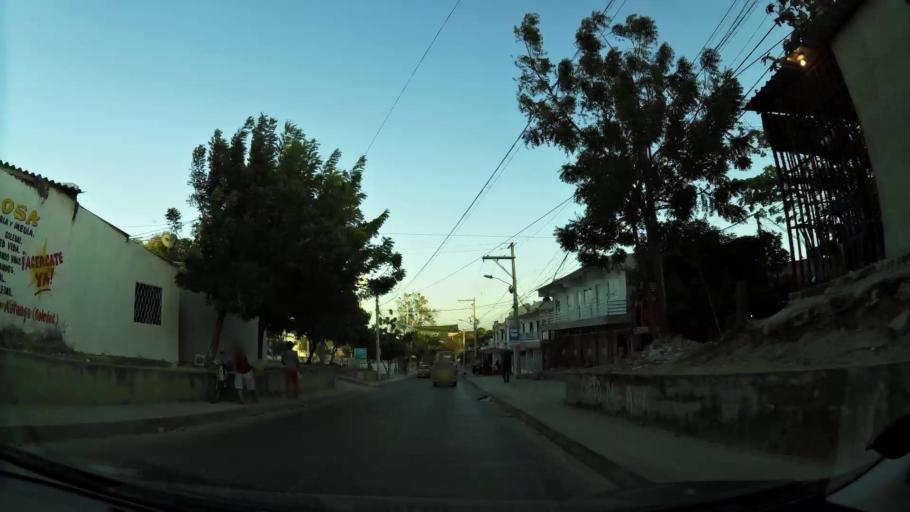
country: CO
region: Atlantico
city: Soledad
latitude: 10.9214
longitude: -74.7951
